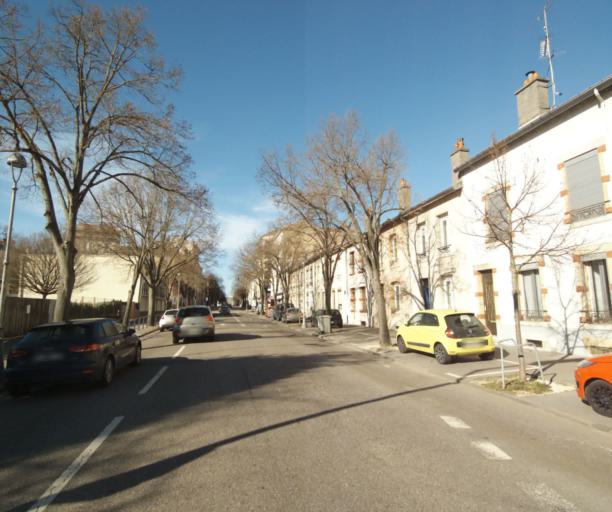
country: FR
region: Lorraine
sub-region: Departement de Meurthe-et-Moselle
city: Nancy
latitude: 48.6749
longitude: 6.1826
